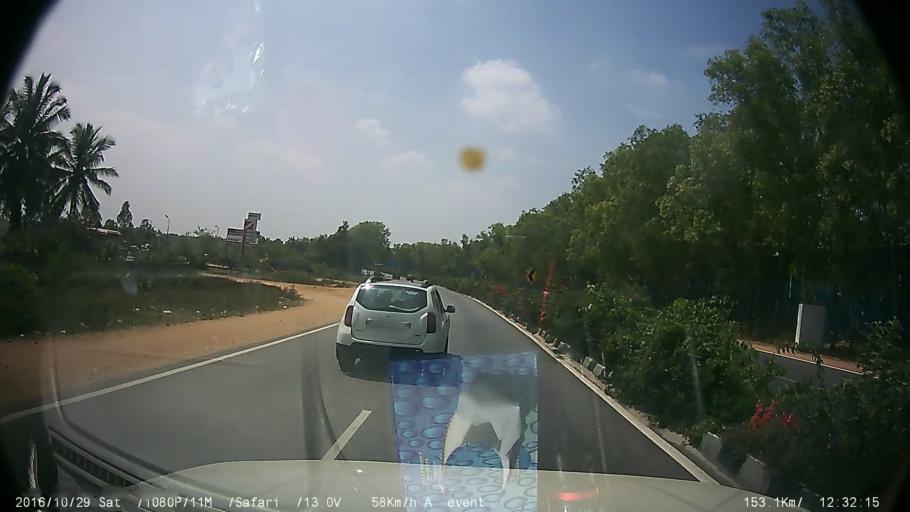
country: IN
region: Karnataka
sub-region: Mysore
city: Mysore
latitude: 12.3538
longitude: 76.5180
